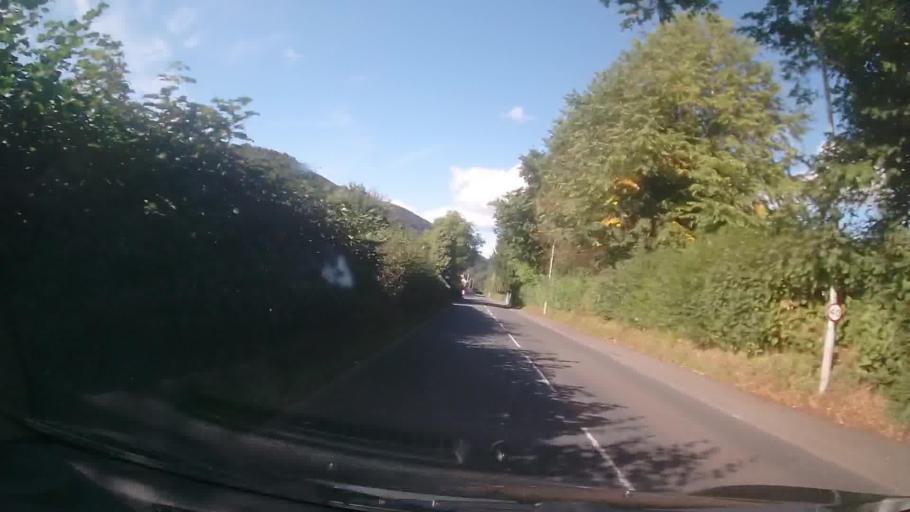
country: GB
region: Wales
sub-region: Blaenau Gwent
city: Brynmawr
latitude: 51.9044
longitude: -3.1938
